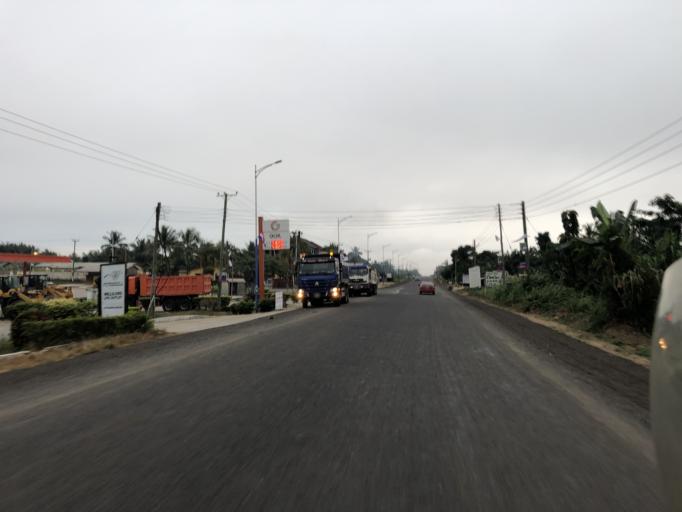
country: GH
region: Eastern
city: Koforidua
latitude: 6.1909
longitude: -0.3572
